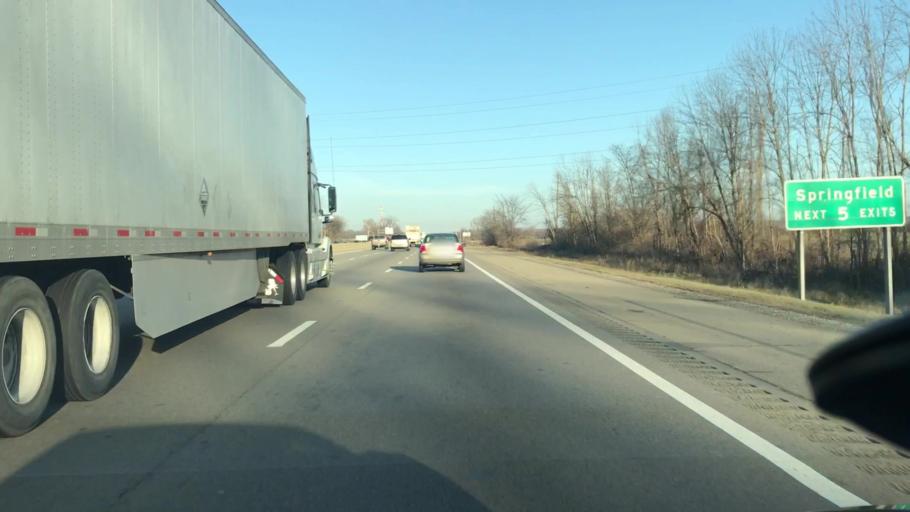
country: US
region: Ohio
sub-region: Clark County
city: Holiday Valley
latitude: 39.8710
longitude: -83.9783
